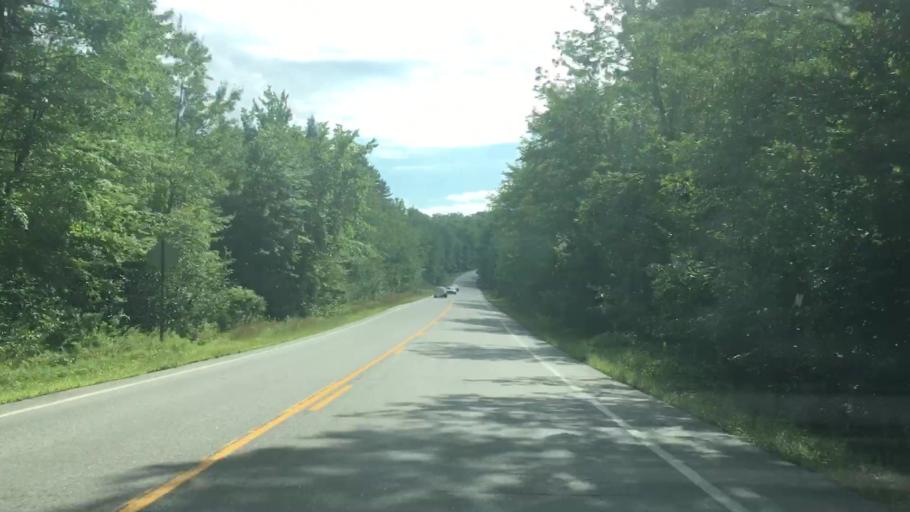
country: US
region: Maine
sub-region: Androscoggin County
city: Poland
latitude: 44.0203
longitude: -70.4410
